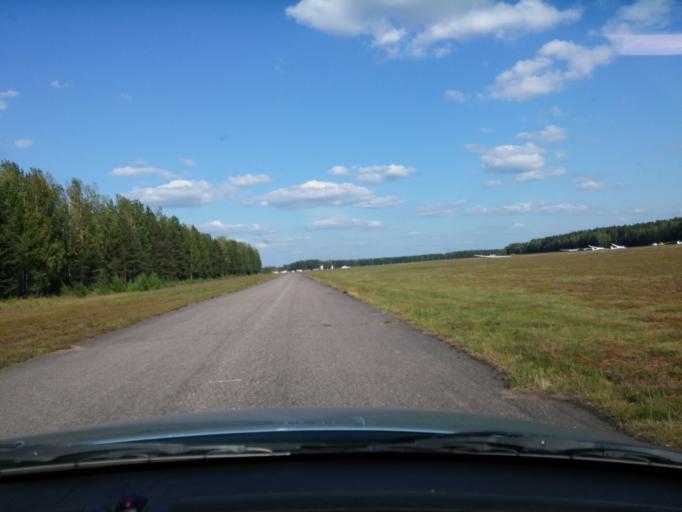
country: FI
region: Uusimaa
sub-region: Helsinki
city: Kaerkoelae
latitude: 60.7419
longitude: 24.0926
